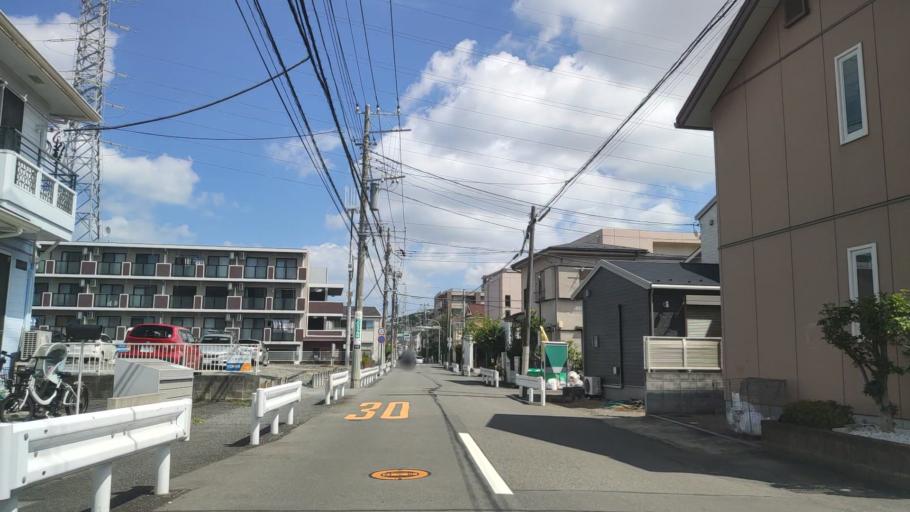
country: JP
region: Kanagawa
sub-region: Kawasaki-shi
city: Kawasaki
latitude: 35.5436
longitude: 139.6373
